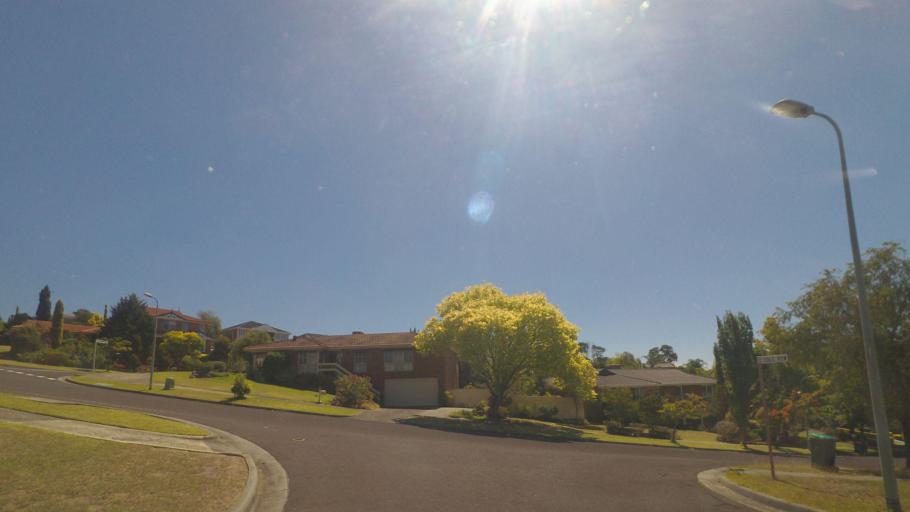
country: AU
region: Victoria
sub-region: Manningham
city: Donvale
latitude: -37.7719
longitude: 145.1798
